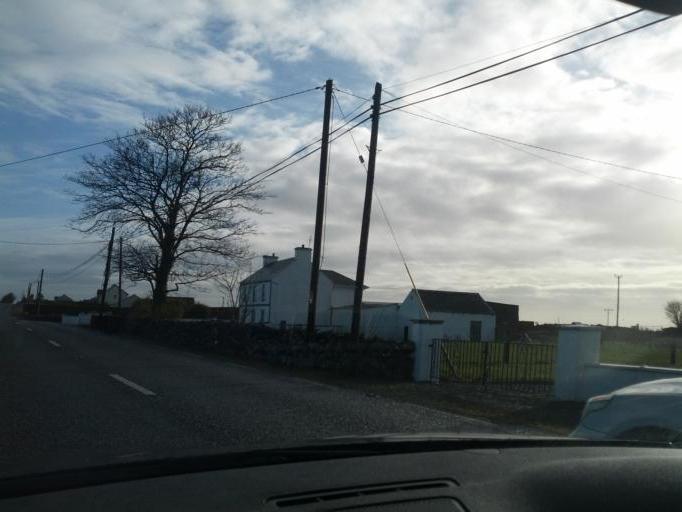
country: IE
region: Connaught
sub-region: County Galway
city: Athenry
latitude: 53.3590
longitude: -8.7345
